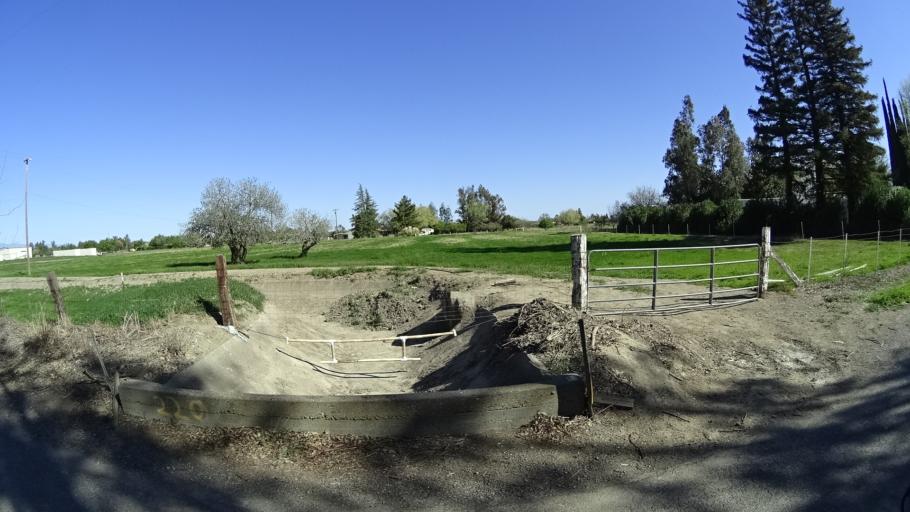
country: US
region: California
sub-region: Glenn County
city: Orland
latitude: 39.7368
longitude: -122.2193
